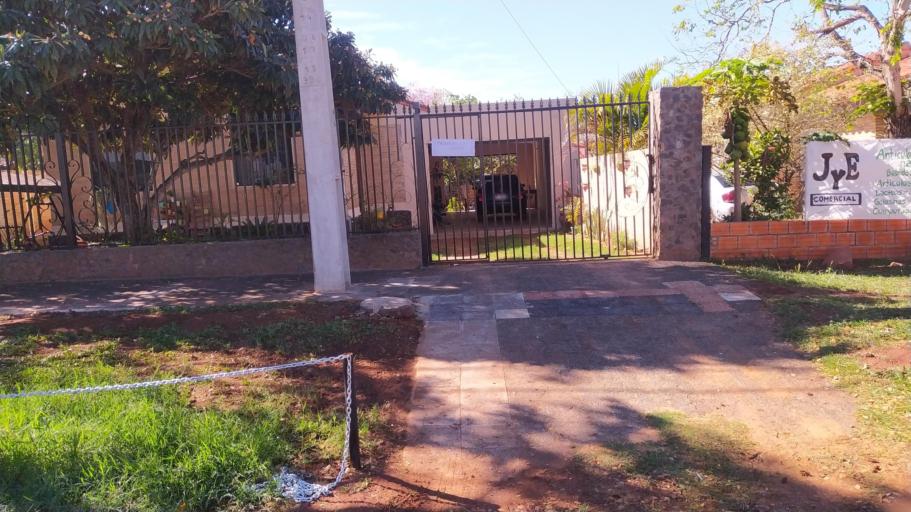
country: PY
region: Misiones
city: San Juan Bautista
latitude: -26.6745
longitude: -57.1386
